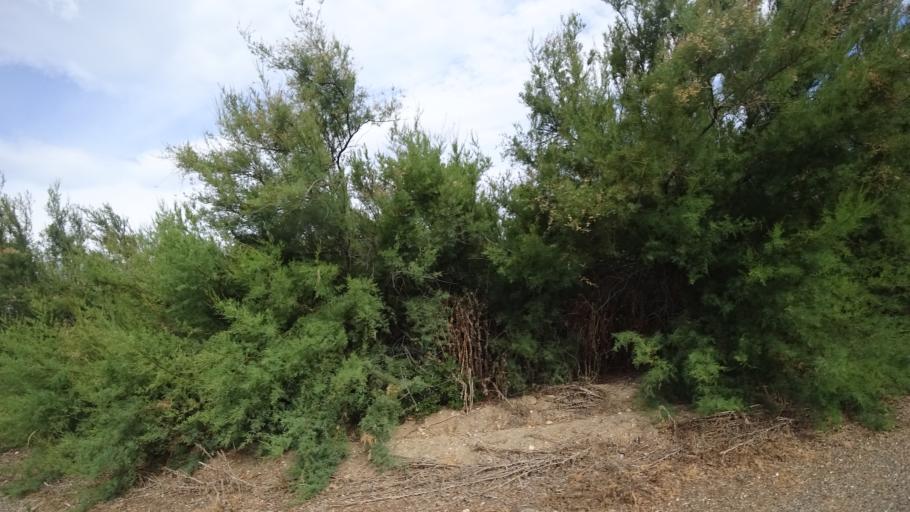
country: FR
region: Languedoc-Roussillon
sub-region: Departement de l'Aude
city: Leucate
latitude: 42.8801
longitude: 3.0439
